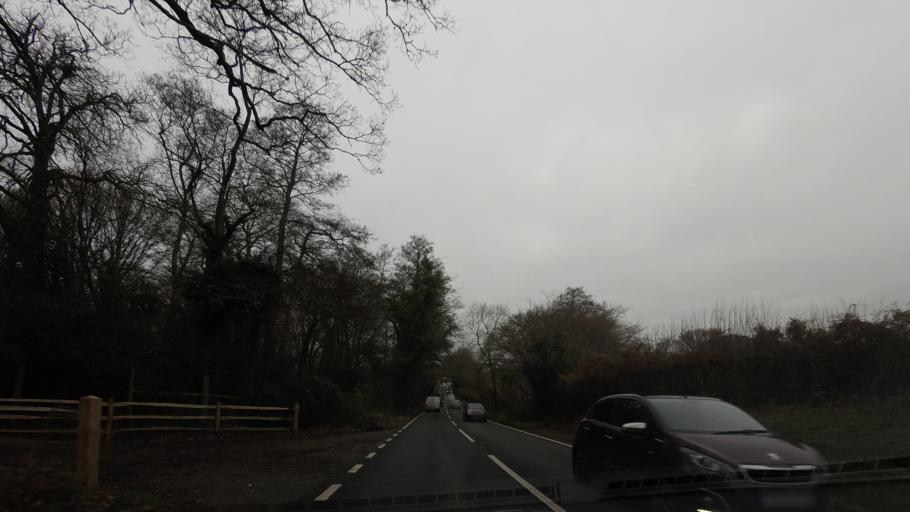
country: GB
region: England
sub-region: East Sussex
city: Saint Leonards-on-Sea
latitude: 50.9059
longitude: 0.5488
